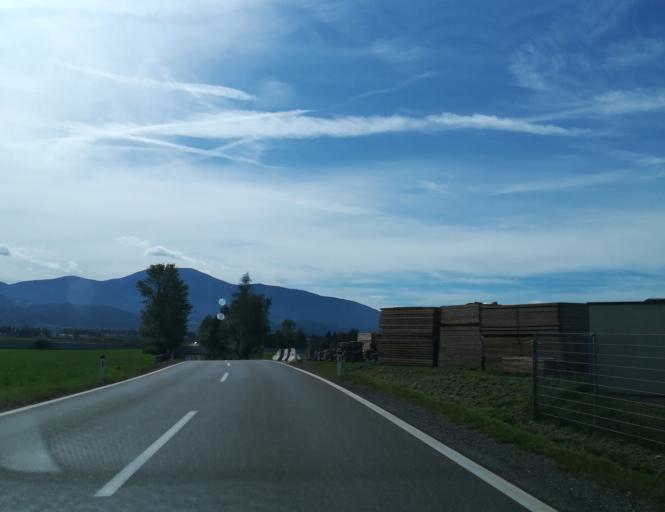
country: AT
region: Styria
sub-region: Politischer Bezirk Murtal
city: Flatschach
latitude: 47.2149
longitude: 14.7554
